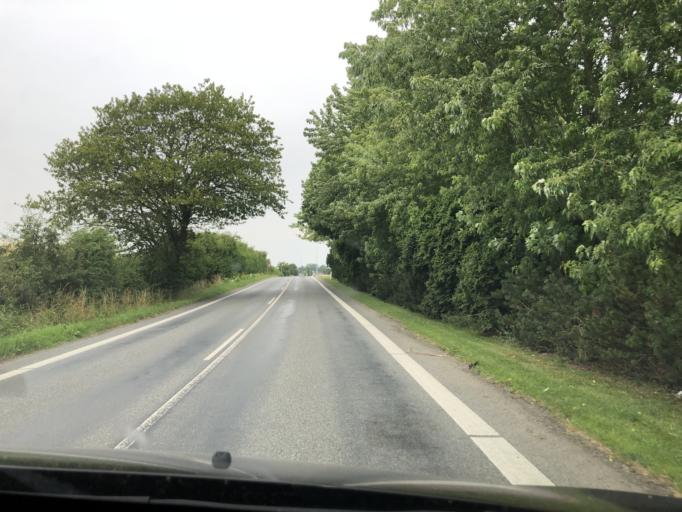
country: DK
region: South Denmark
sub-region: Assens Kommune
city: Harby
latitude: 55.2187
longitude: 10.1359
